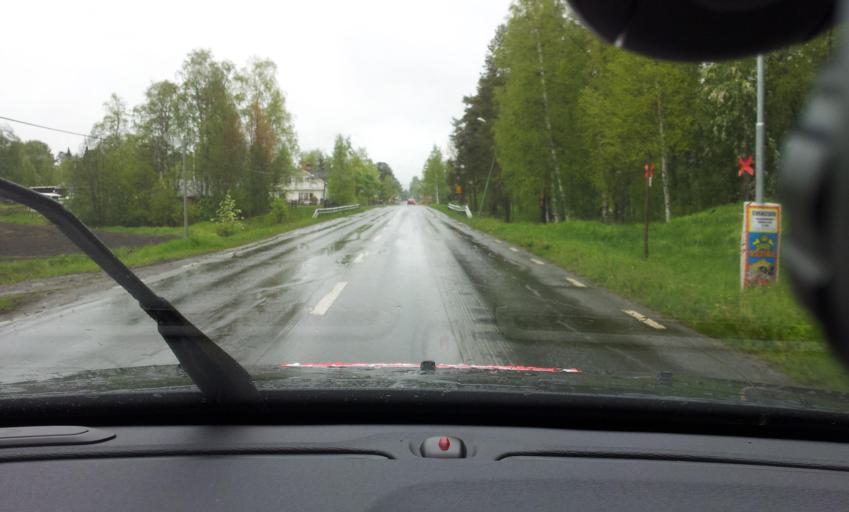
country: SE
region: Jaemtland
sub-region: Bergs Kommun
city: Hoverberg
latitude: 62.7635
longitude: 14.4262
